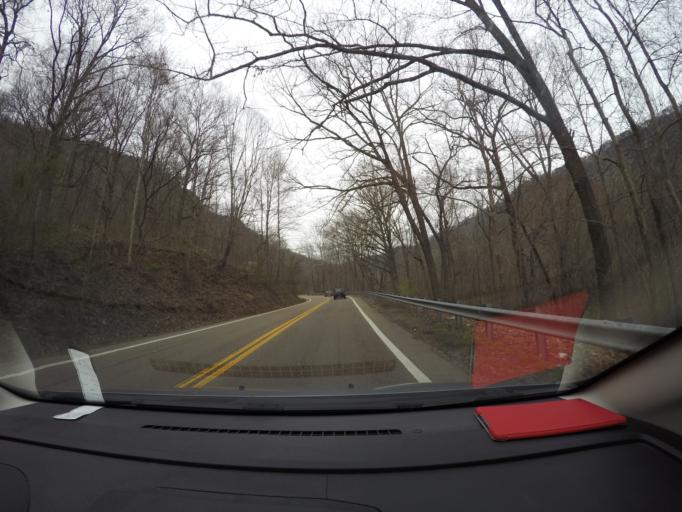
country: US
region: Tennessee
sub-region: Hamilton County
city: Signal Mountain
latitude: 35.1296
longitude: -85.3884
